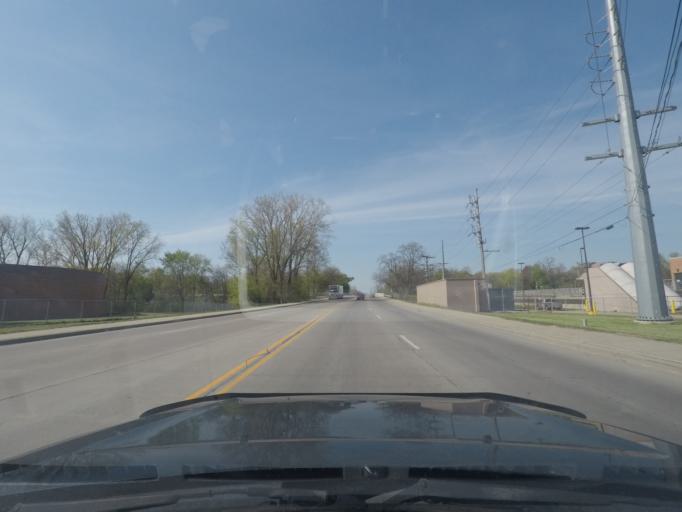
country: US
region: Indiana
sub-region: Elkhart County
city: Elkhart
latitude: 41.6776
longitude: -86.0033
